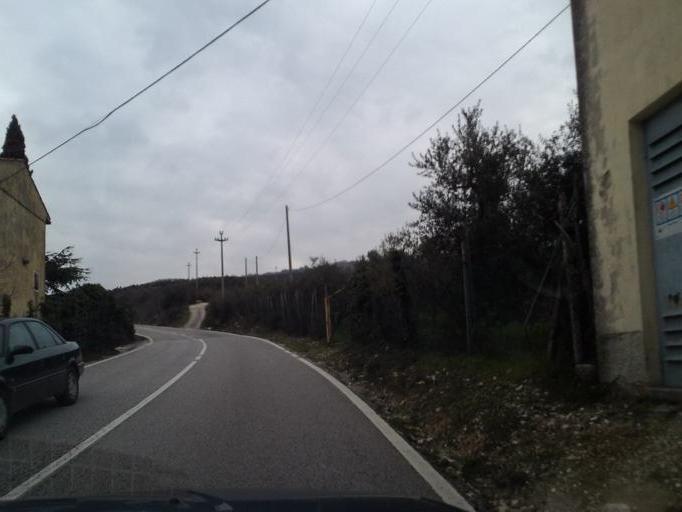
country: IT
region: Veneto
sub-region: Provincia di Verona
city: Montorio
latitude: 45.4883
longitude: 11.0735
